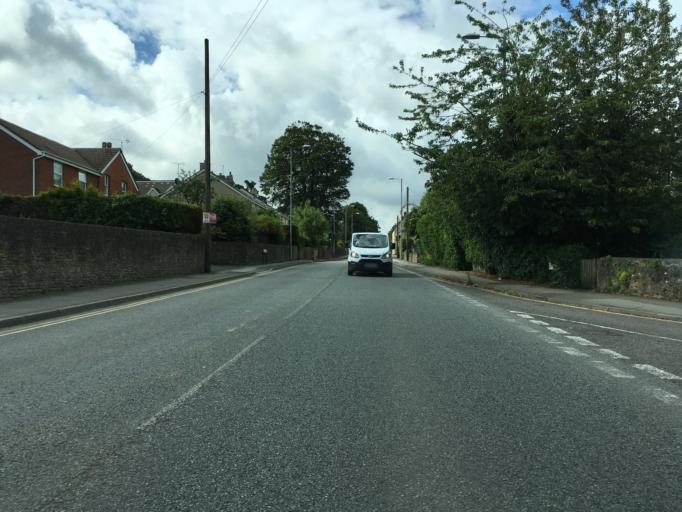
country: GB
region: England
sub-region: Borough of Swindon
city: Highworth
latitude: 51.6329
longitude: -1.7108
